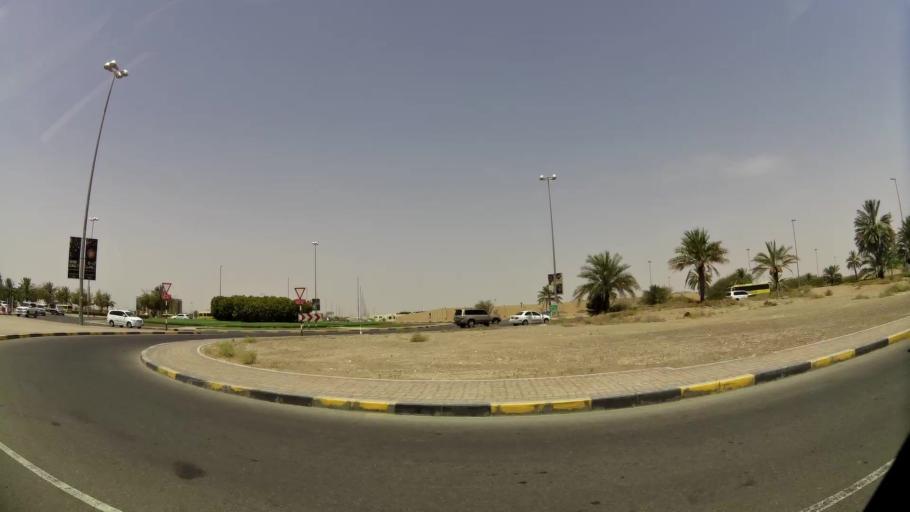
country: AE
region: Abu Dhabi
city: Al Ain
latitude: 24.1957
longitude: 55.7298
